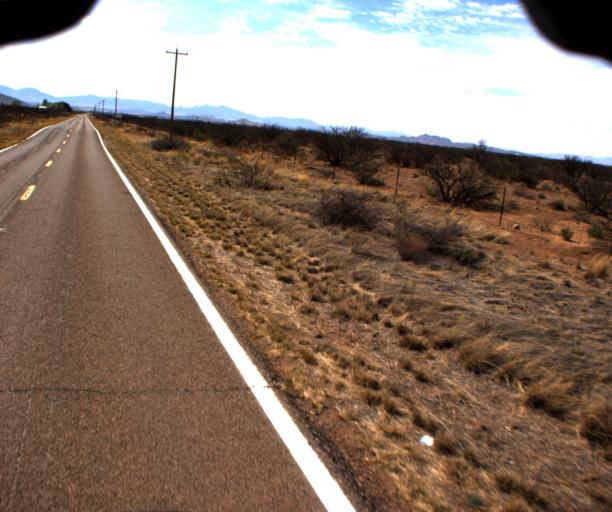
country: US
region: Arizona
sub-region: Cochise County
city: Willcox
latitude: 31.8760
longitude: -109.5681
